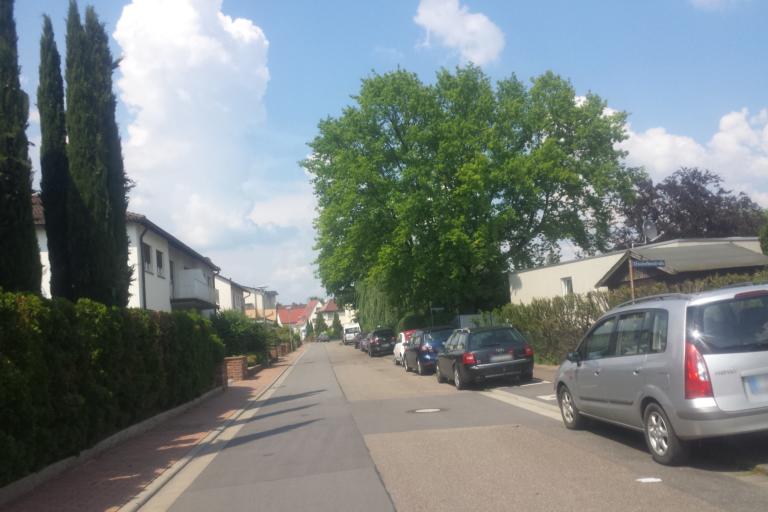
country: DE
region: Baden-Wuerttemberg
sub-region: Karlsruhe Region
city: Edingen-Neckarhausen
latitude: 49.4631
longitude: 8.5965
